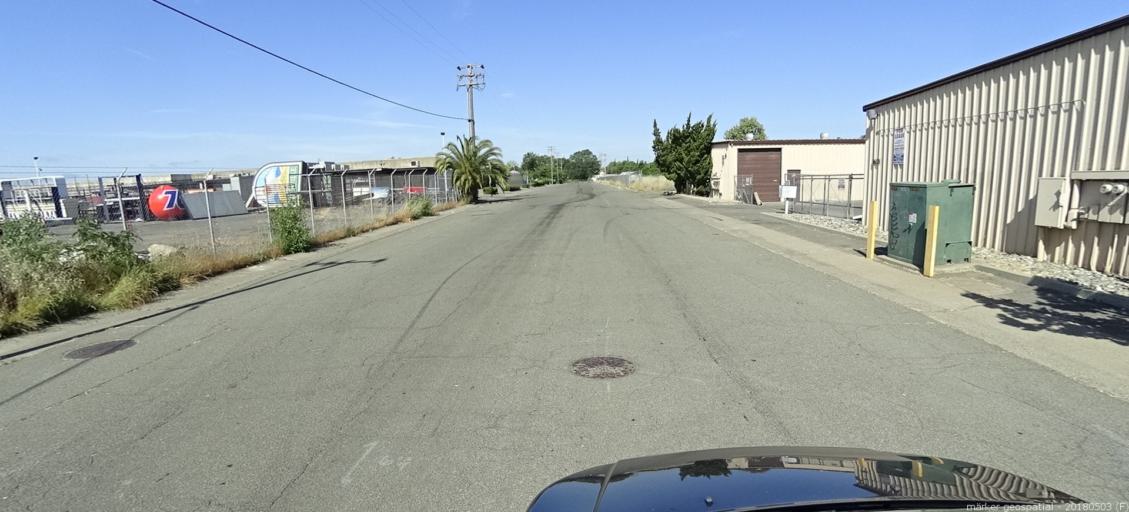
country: US
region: California
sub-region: Sacramento County
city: Arden-Arcade
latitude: 38.6201
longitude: -121.4292
